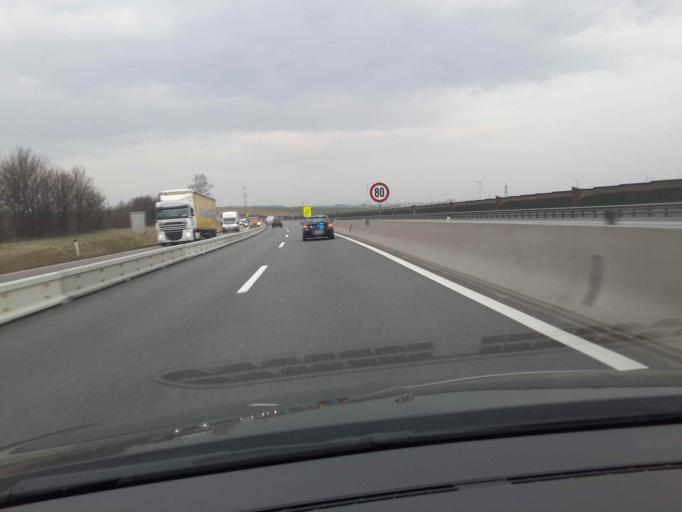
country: AT
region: Lower Austria
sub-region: Politischer Bezirk Sankt Polten
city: Pyhra
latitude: 48.1857
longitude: 15.6838
